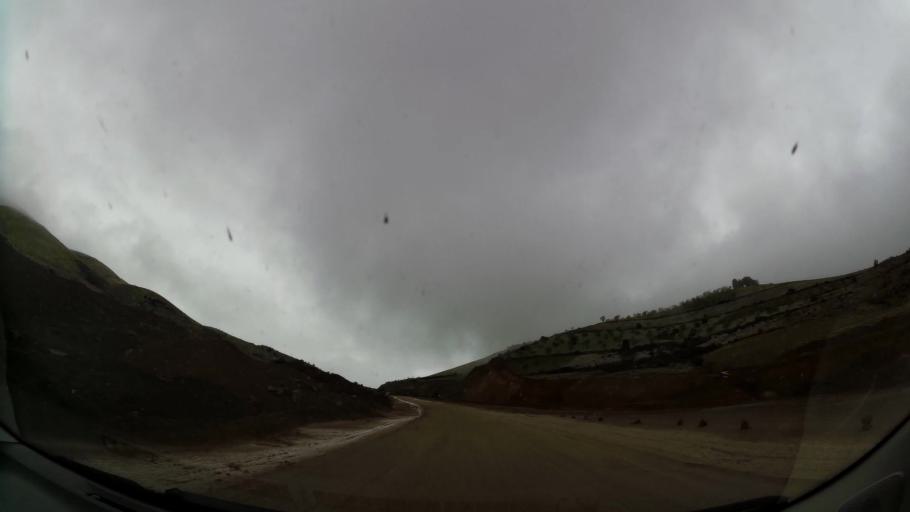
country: MA
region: Taza-Al Hoceima-Taounate
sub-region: Taza
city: Ajdir
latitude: 34.9094
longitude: -3.7964
